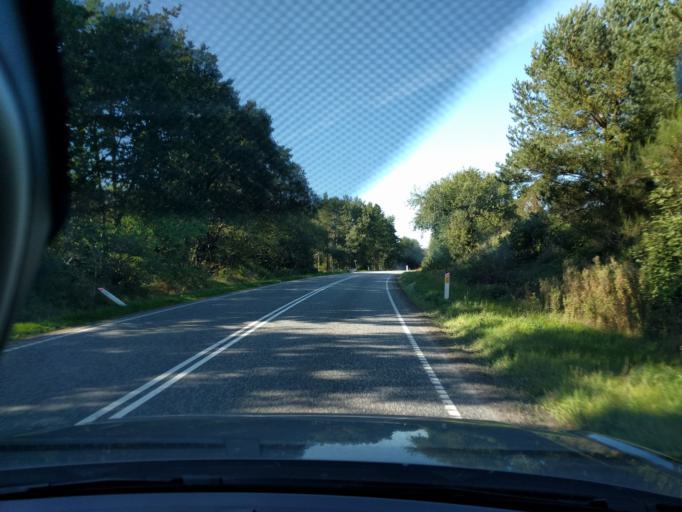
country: DK
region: North Denmark
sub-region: Mariagerfjord Kommune
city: Hobro
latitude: 56.6705
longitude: 9.7046
